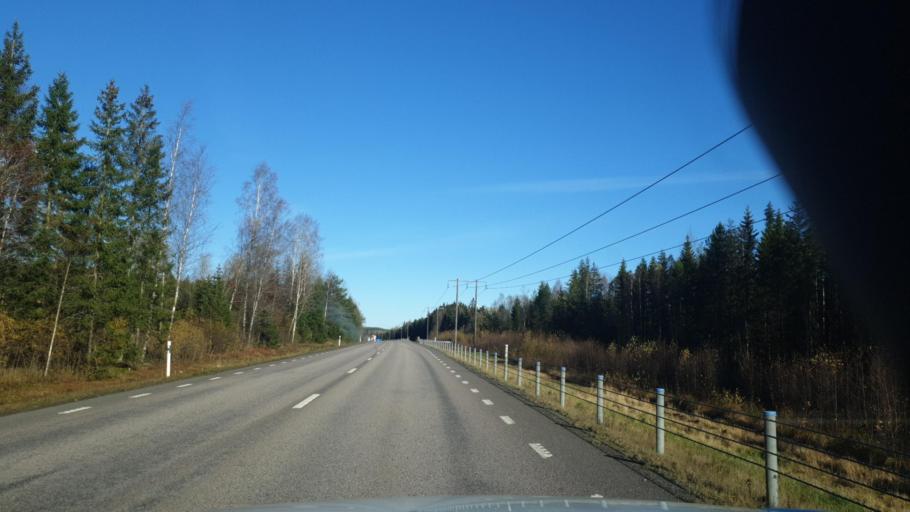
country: SE
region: Vaermland
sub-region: Karlstads Kommun
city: Edsvalla
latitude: 59.4344
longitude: 13.2008
